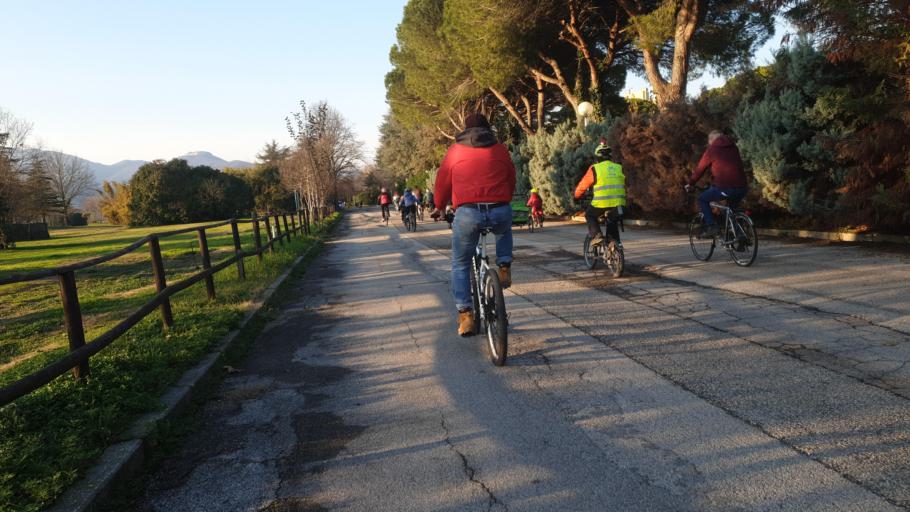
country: IT
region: Veneto
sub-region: Provincia di Padova
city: Battaglia Terme
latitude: 45.2891
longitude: 11.7676
